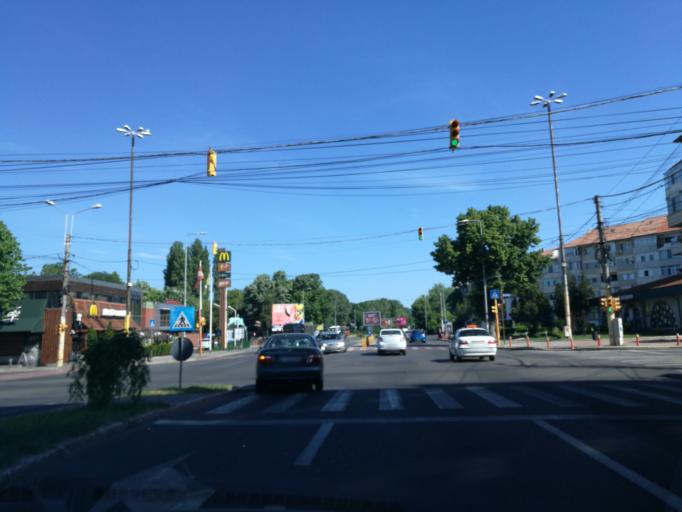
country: RO
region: Constanta
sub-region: Municipiul Constanta
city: Constanta
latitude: 44.2046
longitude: 28.6446
